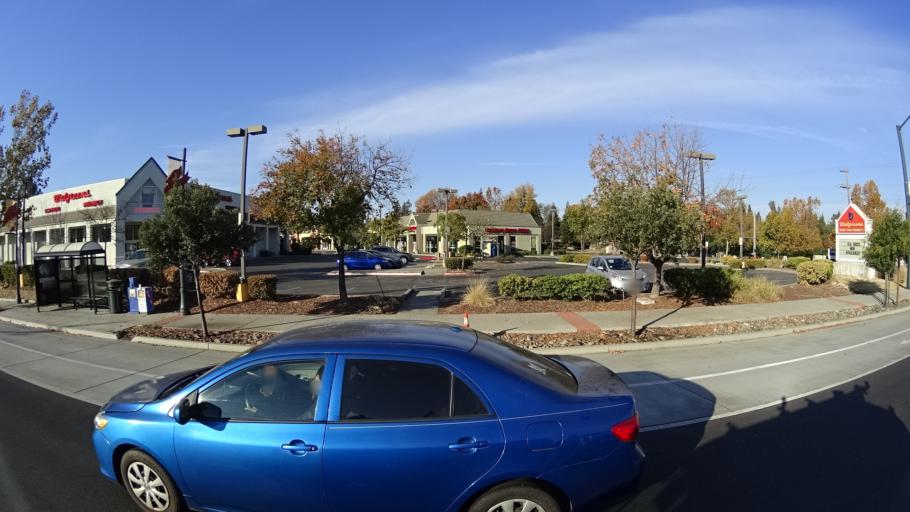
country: US
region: California
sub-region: Sacramento County
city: Citrus Heights
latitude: 38.7073
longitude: -121.2719
